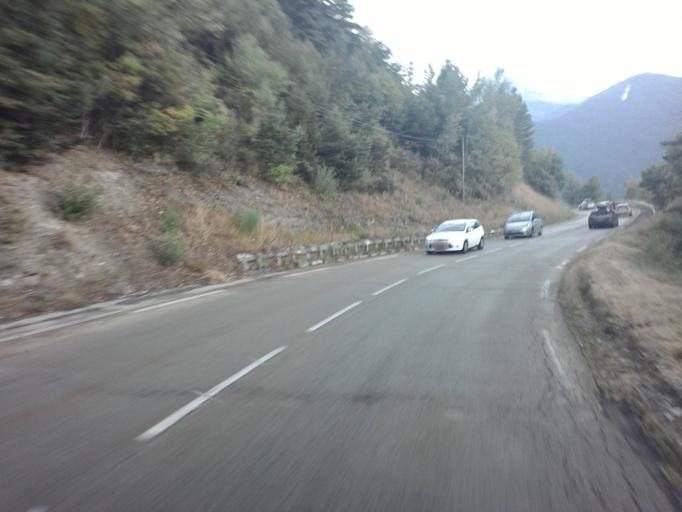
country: FR
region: Provence-Alpes-Cote d'Azur
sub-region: Departement des Hautes-Alpes
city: Saint-Bonnet-en-Champsaur
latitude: 44.8121
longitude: 5.9495
